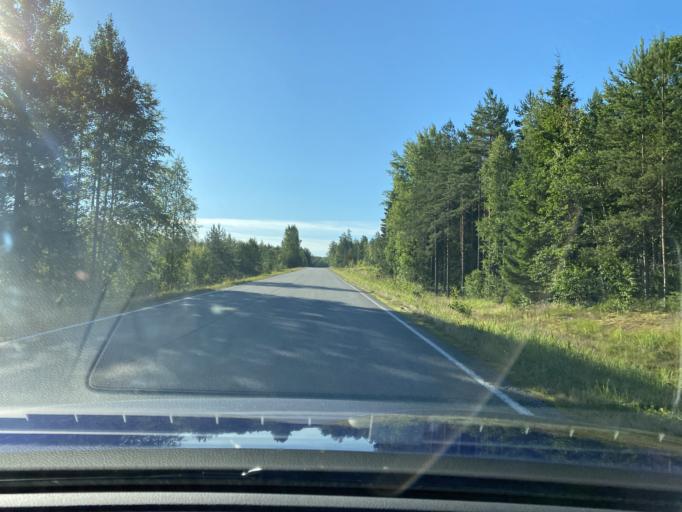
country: FI
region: Haeme
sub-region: Forssa
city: Tammela
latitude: 60.9219
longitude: 23.8250
